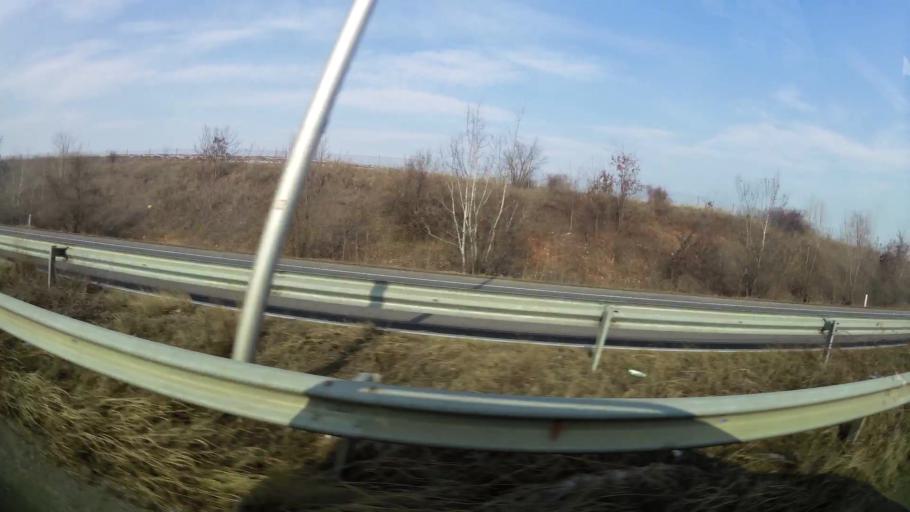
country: MK
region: Butel
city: Butel
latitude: 42.0327
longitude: 21.4787
